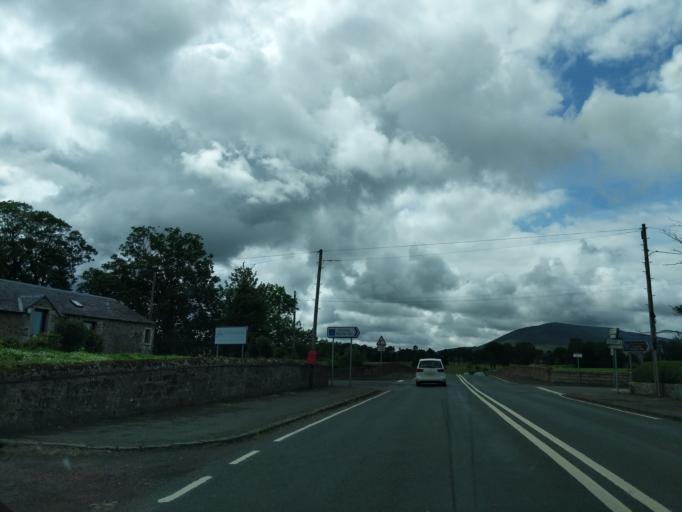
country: GB
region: Scotland
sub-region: South Lanarkshire
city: Biggar
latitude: 55.6096
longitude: -3.5580
